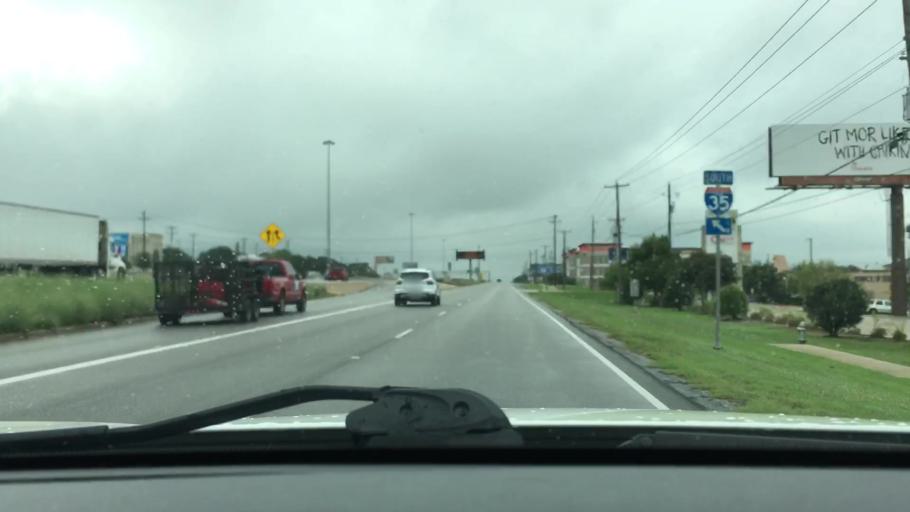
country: US
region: Texas
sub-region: Travis County
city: Wells Branch
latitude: 30.4315
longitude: -97.6706
